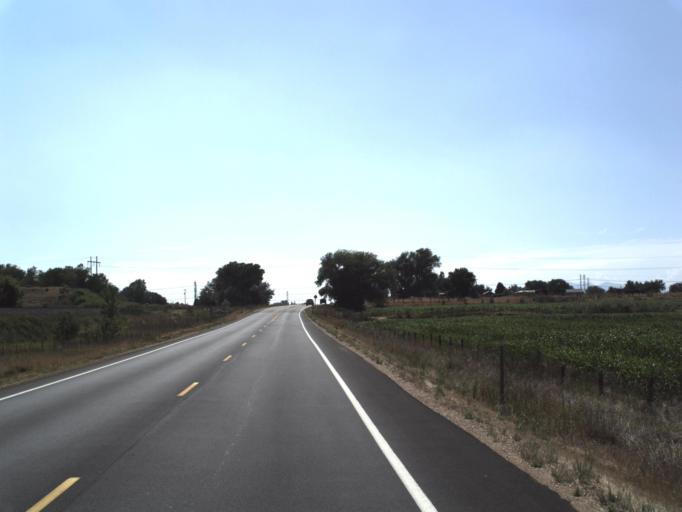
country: US
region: Utah
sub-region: Weber County
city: Marriott-Slaterville
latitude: 41.2449
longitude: -112.0381
